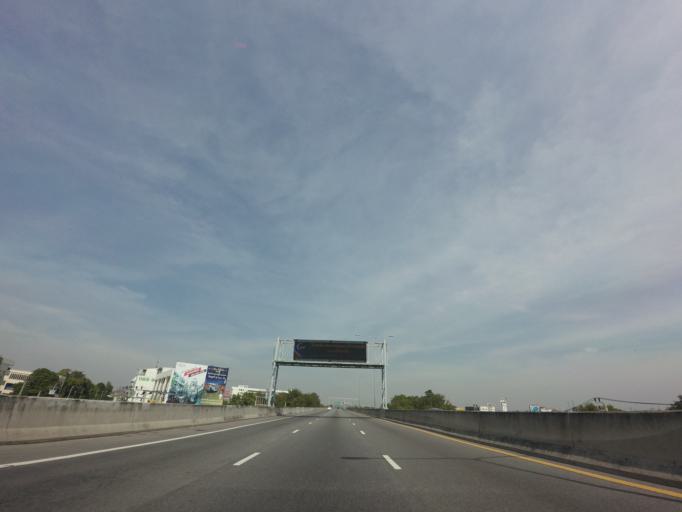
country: TH
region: Bangkok
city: Bang Khen
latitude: 13.8680
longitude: 100.6457
